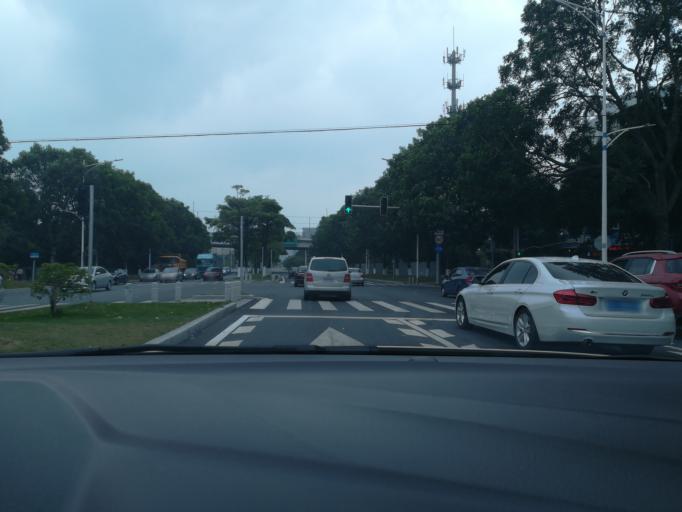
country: CN
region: Guangdong
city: Nansha
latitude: 22.7827
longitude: 113.5924
